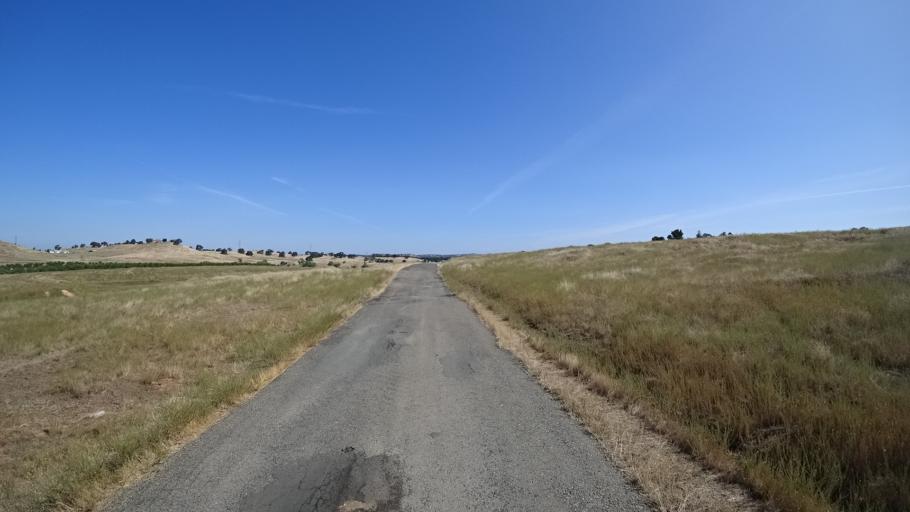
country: US
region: California
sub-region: Calaveras County
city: Rancho Calaveras
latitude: 38.0801
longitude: -120.9108
